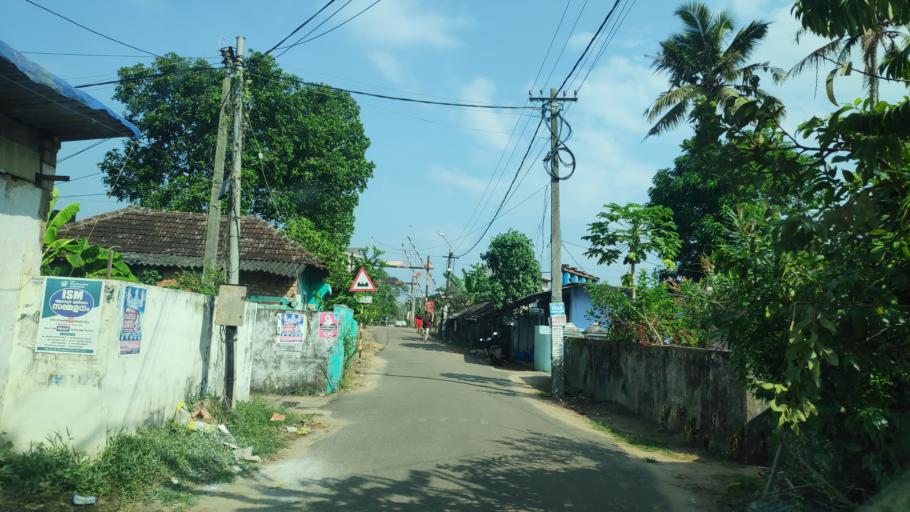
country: IN
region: Kerala
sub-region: Alappuzha
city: Alleppey
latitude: 9.5002
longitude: 76.3181
